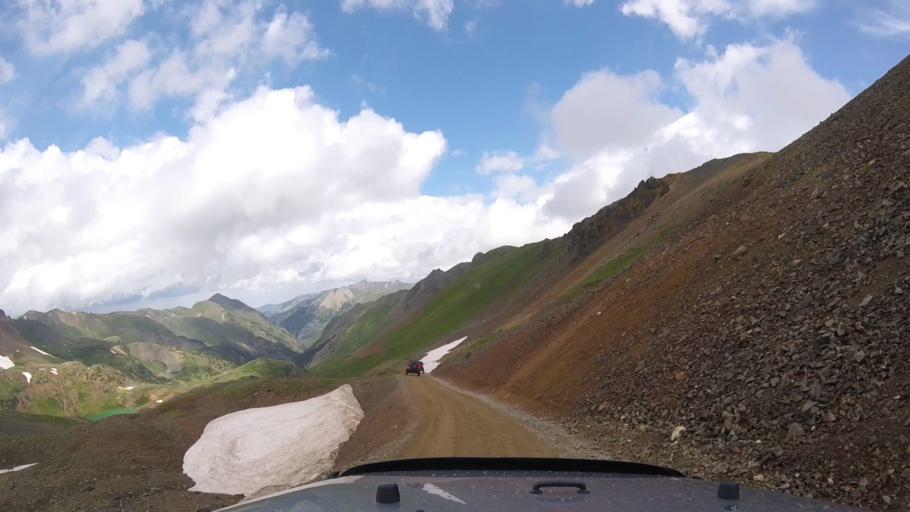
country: US
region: Colorado
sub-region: San Juan County
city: Silverton
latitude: 37.9174
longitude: -107.6188
